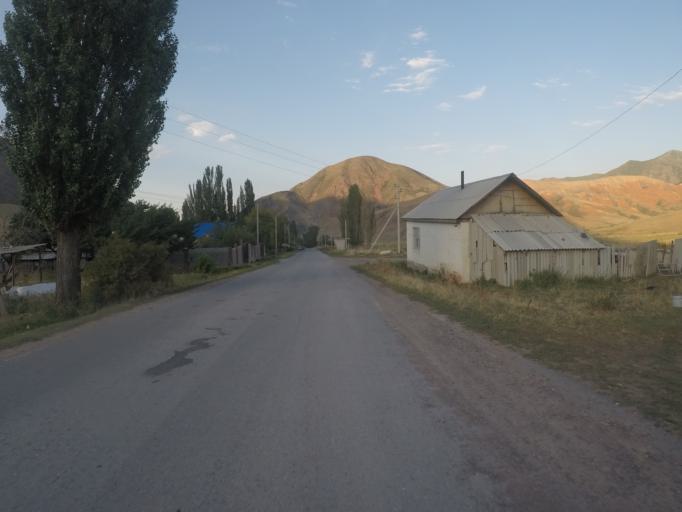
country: KG
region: Chuy
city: Bishkek
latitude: 42.6717
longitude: 74.6488
